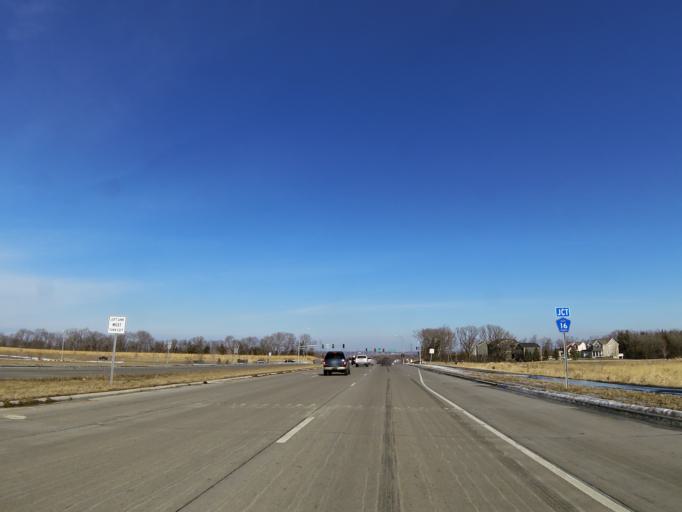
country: US
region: Minnesota
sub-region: Scott County
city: Prior Lake
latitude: 44.7659
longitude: -93.4367
